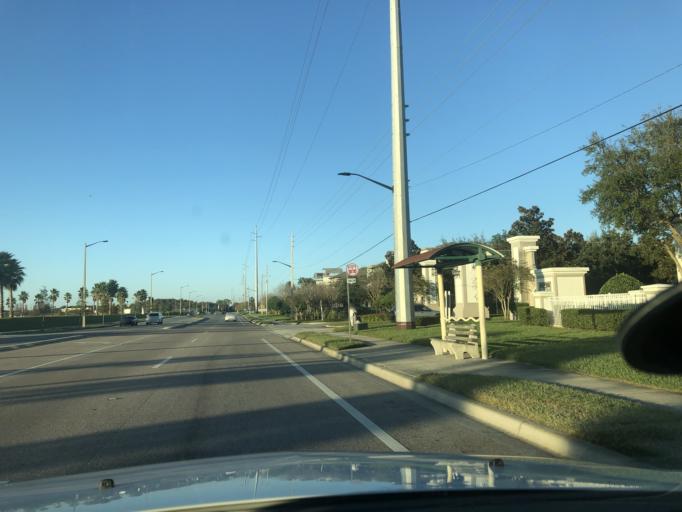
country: US
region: Florida
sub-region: Orange County
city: Oak Ridge
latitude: 28.4774
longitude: -81.4422
